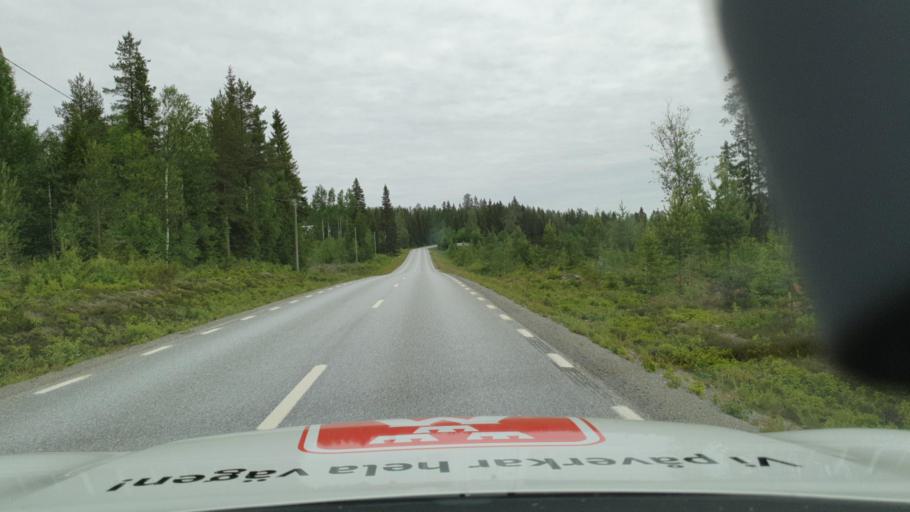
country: SE
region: Vaesterbotten
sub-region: Skelleftea Kommun
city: Burtraesk
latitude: 64.3905
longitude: 20.2891
